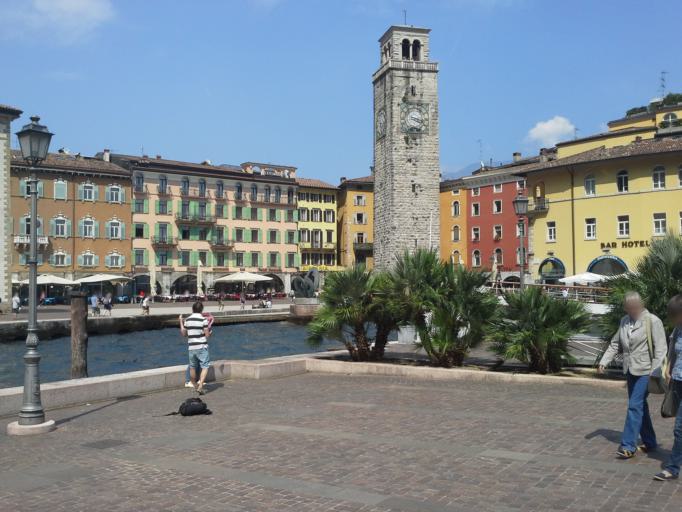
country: IT
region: Trentino-Alto Adige
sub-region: Provincia di Trento
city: Riva del Garda
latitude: 45.8843
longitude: 10.8391
